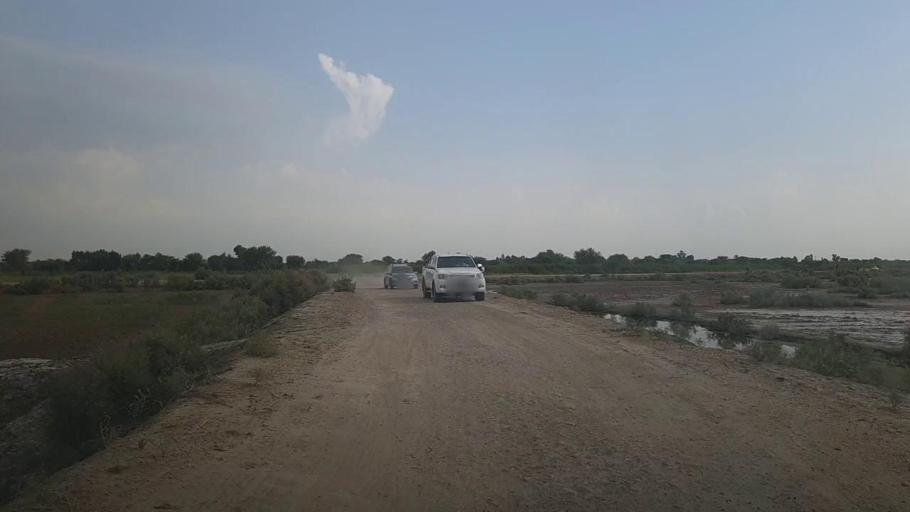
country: PK
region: Sindh
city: Mirpur Mathelo
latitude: 27.9108
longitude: 69.5115
